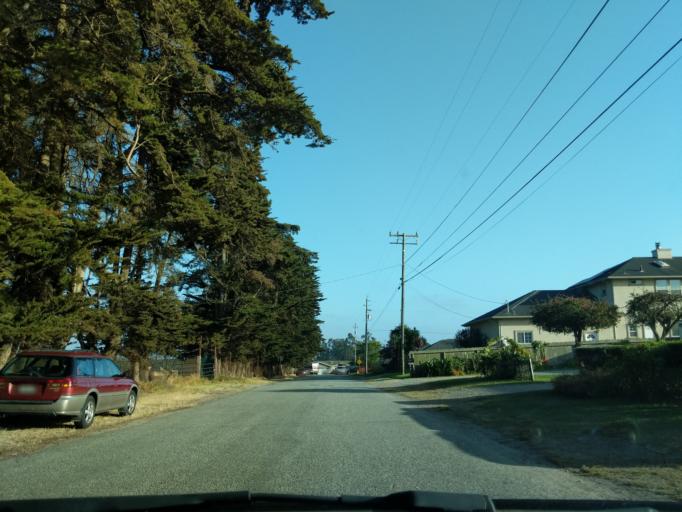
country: US
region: California
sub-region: Monterey County
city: Las Lomas
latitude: 36.8683
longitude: -121.7600
